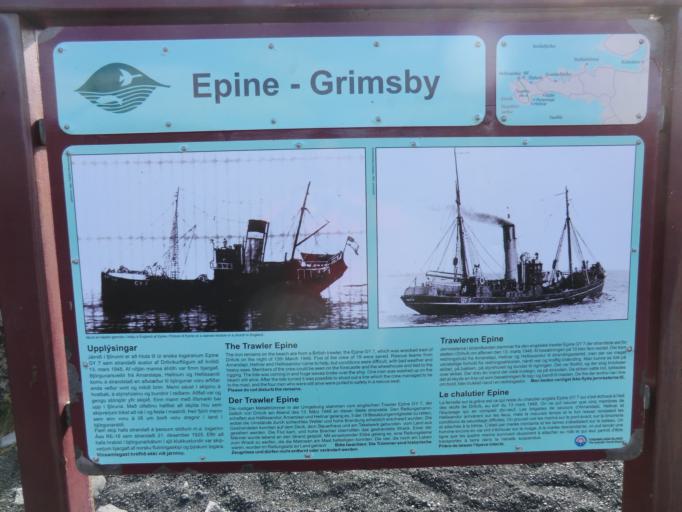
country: IS
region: West
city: Olafsvik
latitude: 64.7531
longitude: -23.8990
